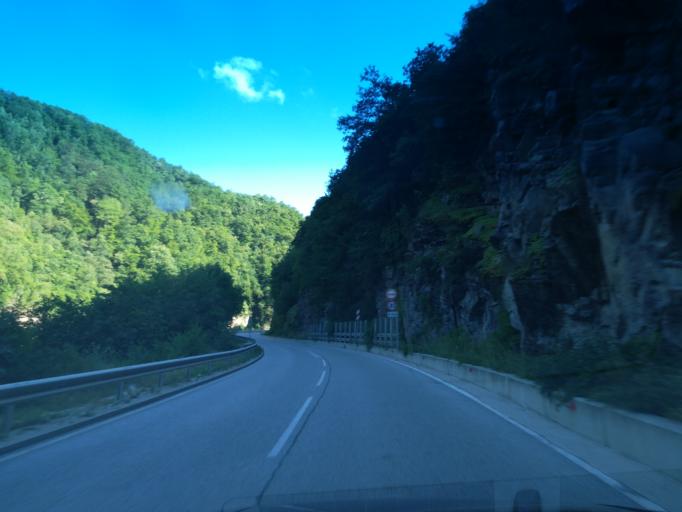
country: BG
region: Smolyan
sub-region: Obshtina Chepelare
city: Chepelare
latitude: 41.8004
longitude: 24.7098
